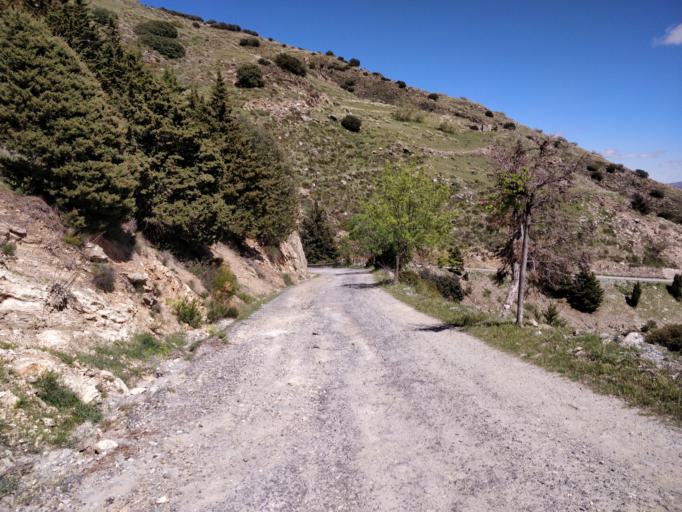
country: ES
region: Andalusia
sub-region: Provincia de Granada
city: Soportujar
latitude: 36.9355
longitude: -3.4033
